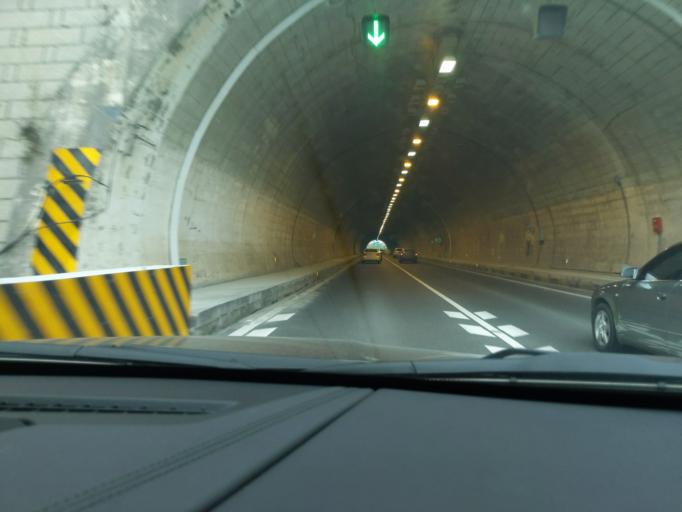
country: CN
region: Fujian
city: Dongshi
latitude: 24.7017
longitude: 118.3760
